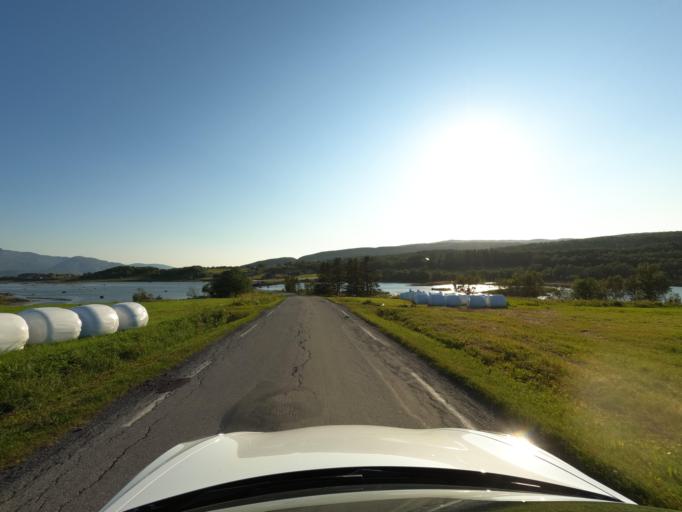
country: NO
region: Troms
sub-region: Skanland
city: Evenskjer
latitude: 68.4651
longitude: 16.6531
